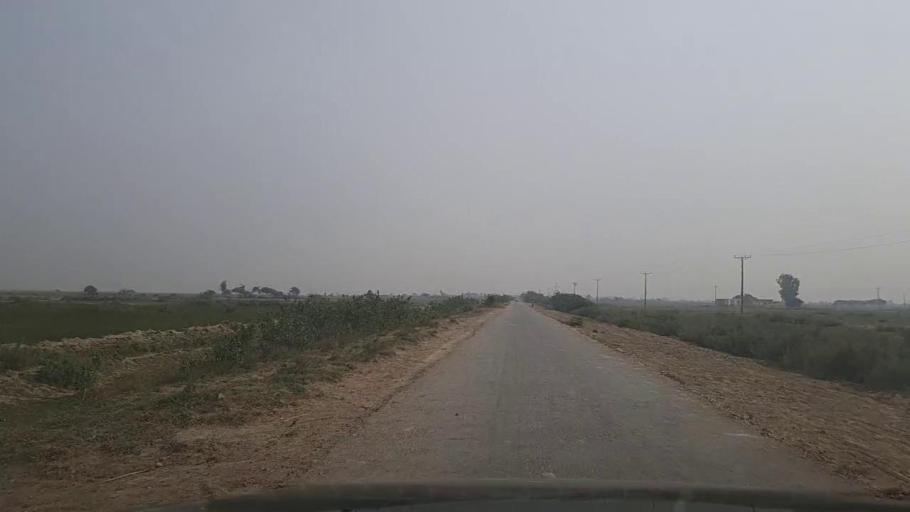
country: PK
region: Sindh
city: Mirpur Sakro
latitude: 24.4778
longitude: 67.6609
